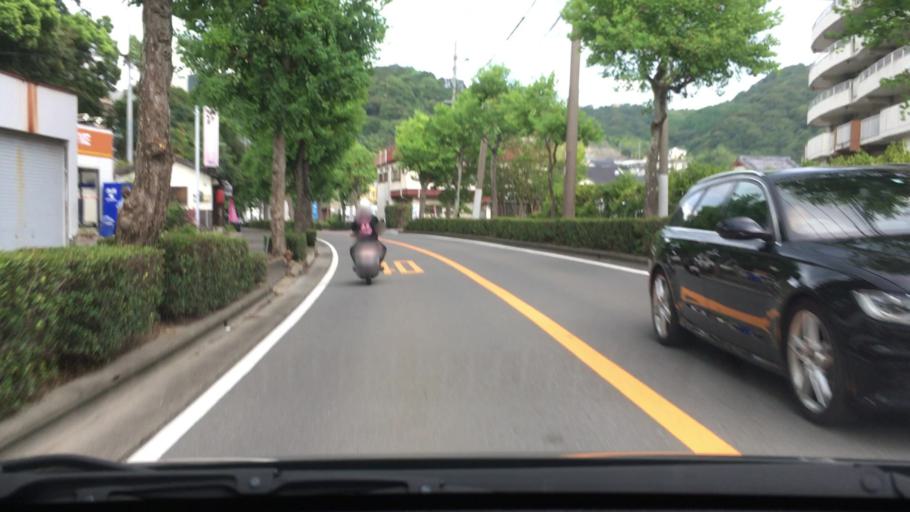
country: JP
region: Nagasaki
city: Togitsu
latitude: 32.8281
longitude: 129.7794
